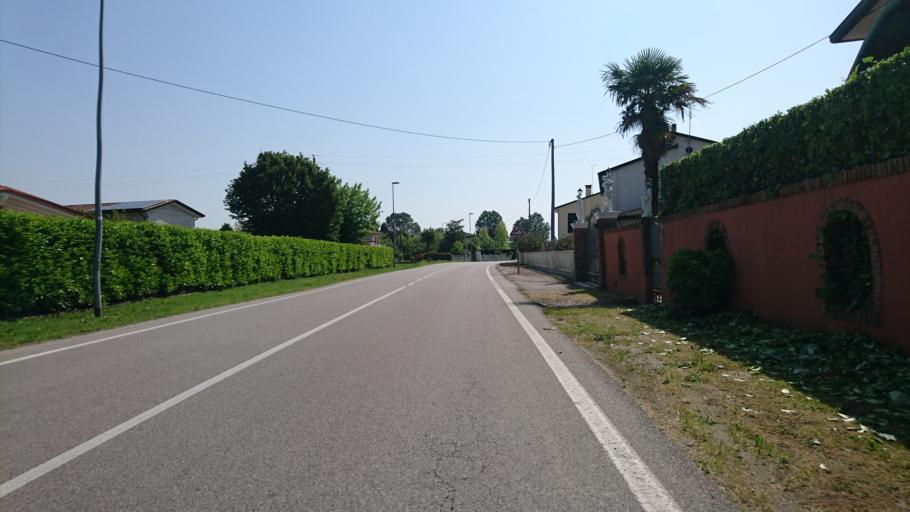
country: IT
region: Veneto
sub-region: Provincia di Venezia
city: Campagna Lupia
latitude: 45.3609
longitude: 12.1111
